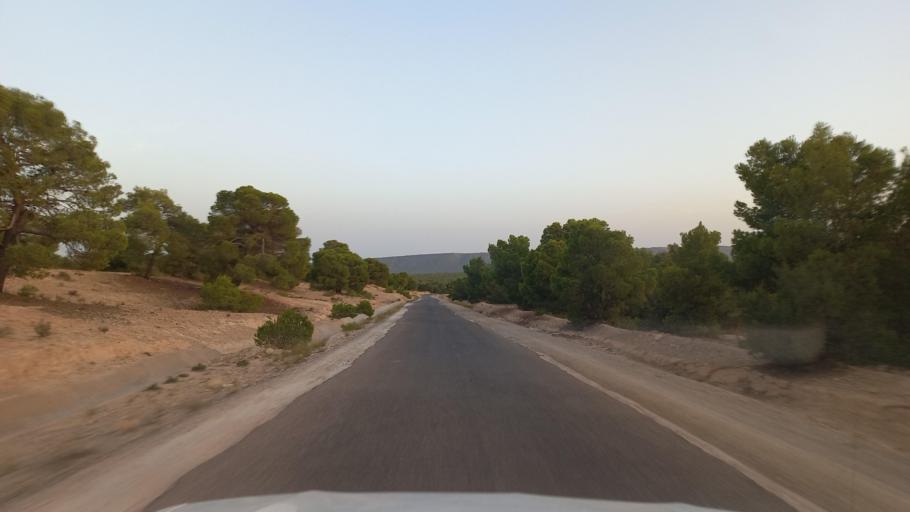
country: TN
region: Al Qasrayn
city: Sbiba
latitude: 35.4201
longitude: 8.9243
